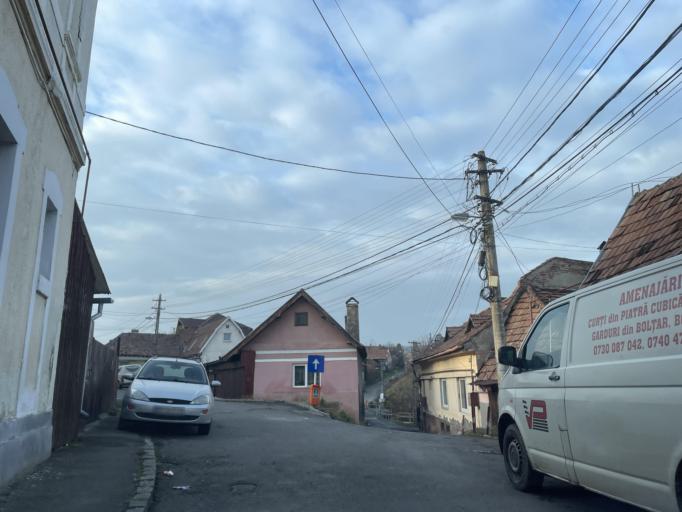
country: RO
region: Mures
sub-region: Municipiul Reghin
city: Reghin
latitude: 46.7838
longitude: 24.7034
